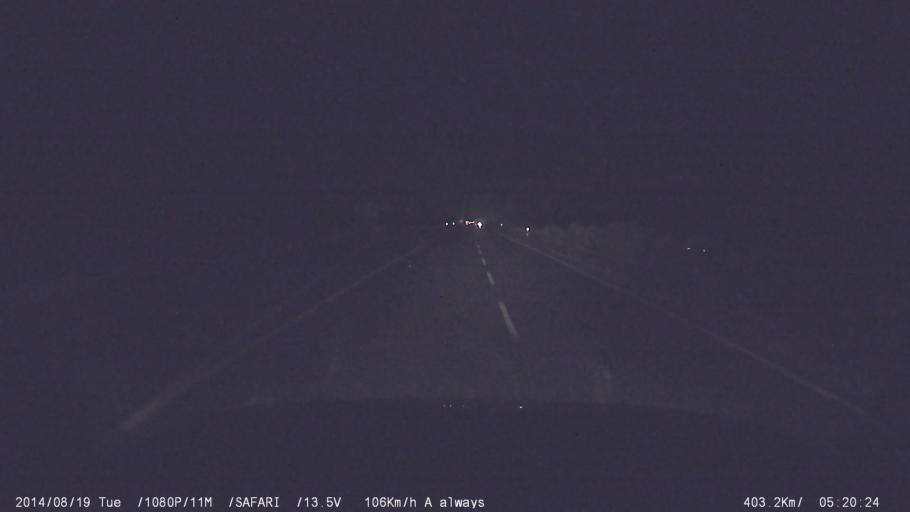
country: IN
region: Tamil Nadu
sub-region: Salem
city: Konganapuram
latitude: 11.5388
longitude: 77.9699
